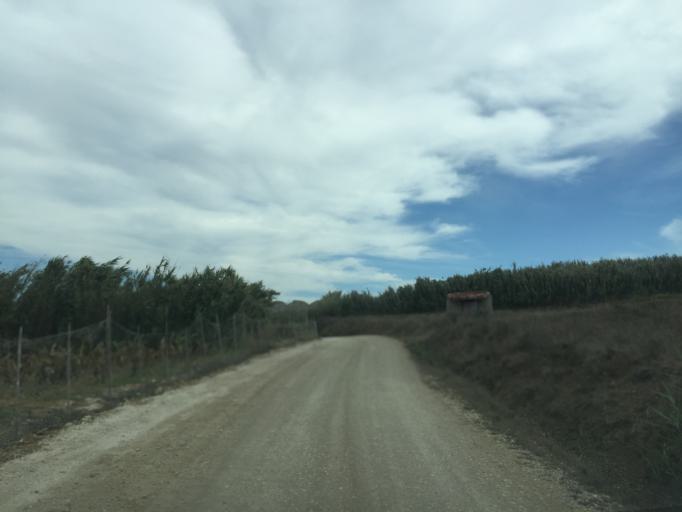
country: PT
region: Lisbon
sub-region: Lourinha
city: Lourinha
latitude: 39.1949
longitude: -9.3416
